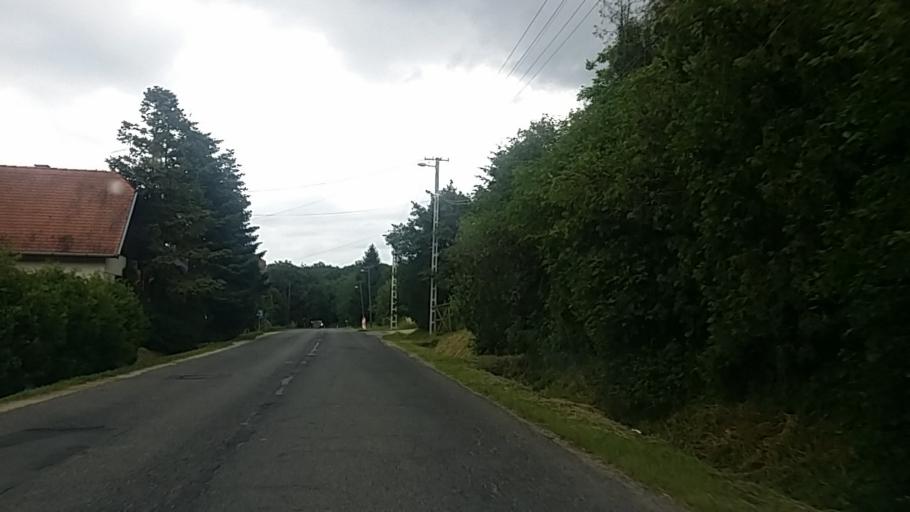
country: SI
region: Hodos-Hodos
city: Hodos
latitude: 46.8366
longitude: 16.4248
